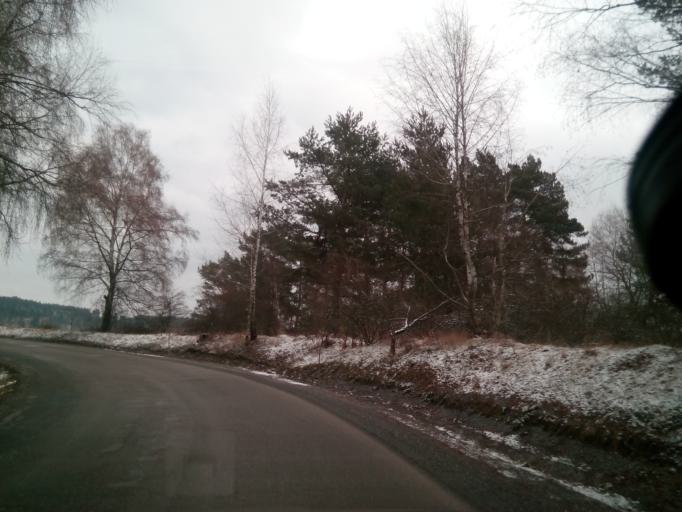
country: SK
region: Presovsky
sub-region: Okres Presov
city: Levoca
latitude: 49.0216
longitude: 20.6238
